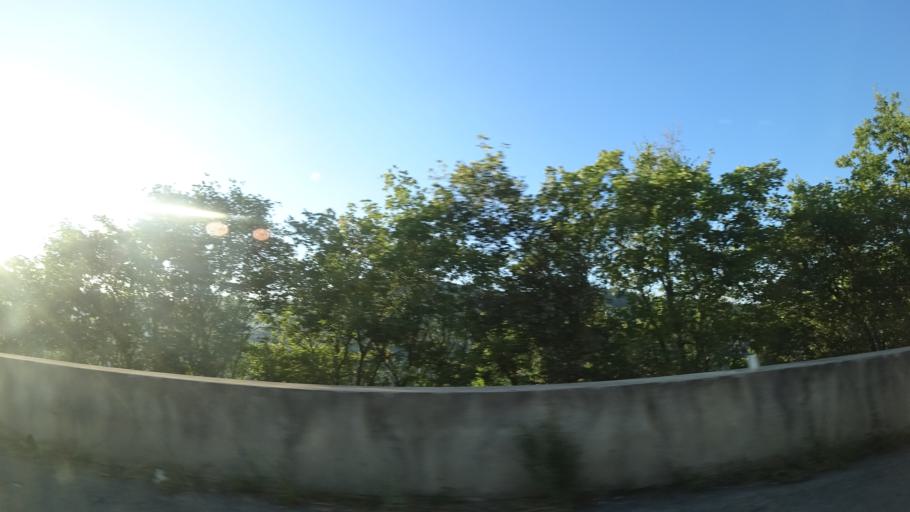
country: FR
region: Midi-Pyrenees
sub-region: Departement de l'Aveyron
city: Millau
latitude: 44.0928
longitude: 3.1093
